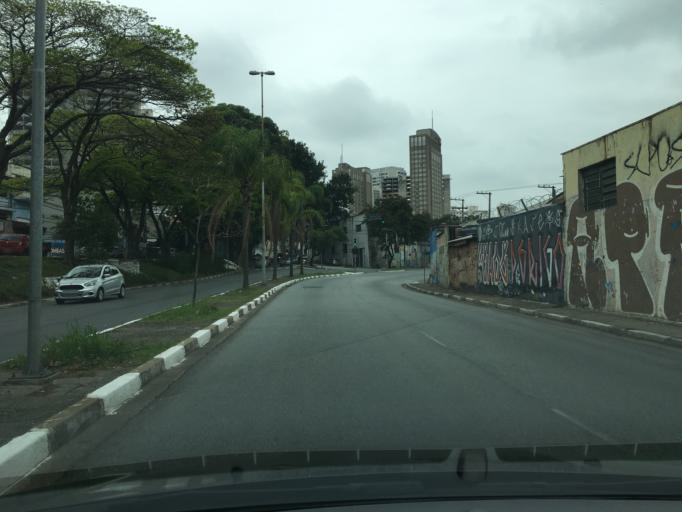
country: BR
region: Sao Paulo
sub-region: Guarulhos
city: Guarulhos
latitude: -23.4759
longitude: -46.5347
